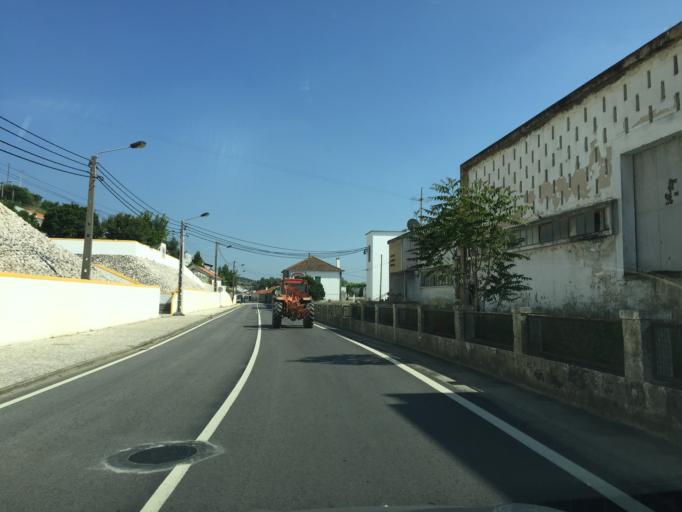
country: PT
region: Santarem
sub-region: Golega
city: Golega
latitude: 39.3506
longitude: -8.4846
